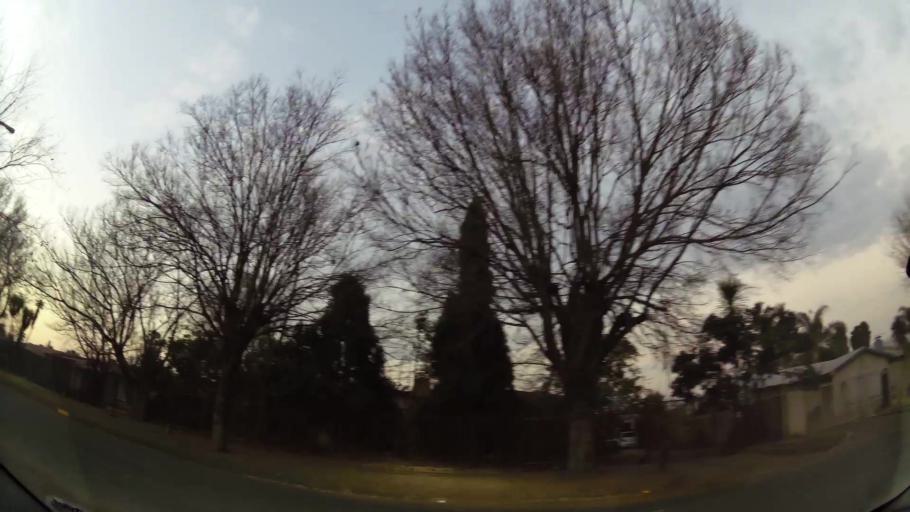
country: ZA
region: Gauteng
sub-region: Ekurhuleni Metropolitan Municipality
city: Benoni
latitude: -26.1442
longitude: 28.3095
